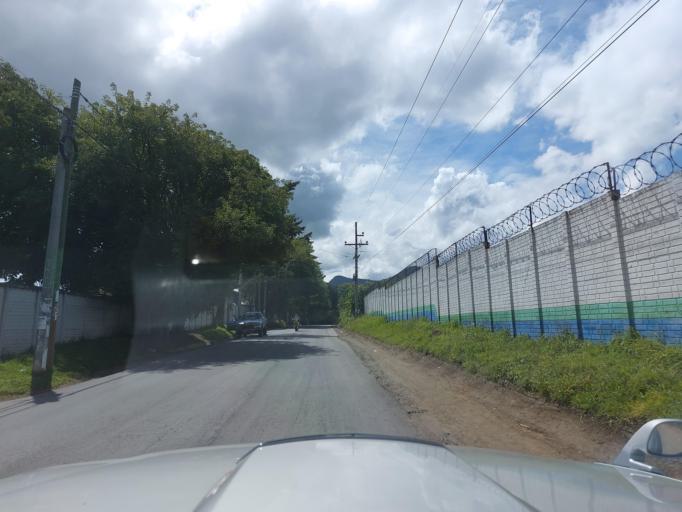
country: GT
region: Chimaltenango
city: Parramos
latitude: 14.6095
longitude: -90.8124
